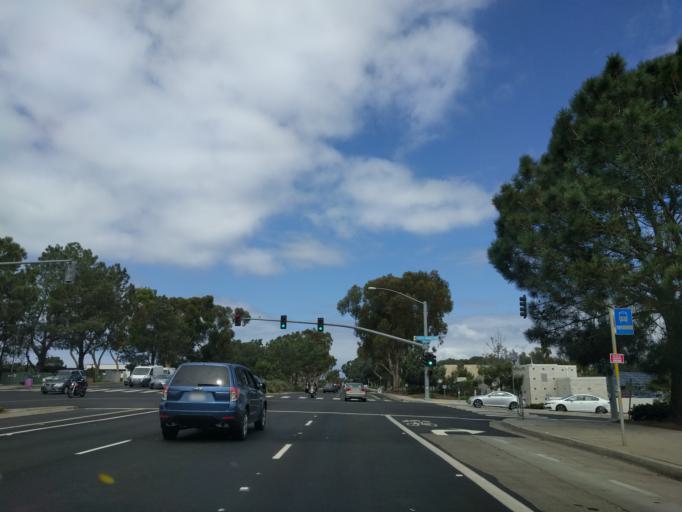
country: US
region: California
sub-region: San Diego County
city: La Jolla
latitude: 32.8978
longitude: -117.2418
